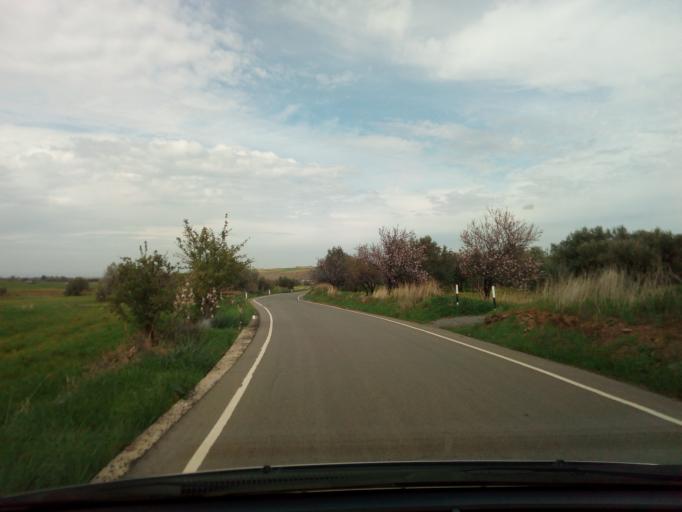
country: CY
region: Lefkosia
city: Astromeritis
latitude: 35.0896
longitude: 32.9949
